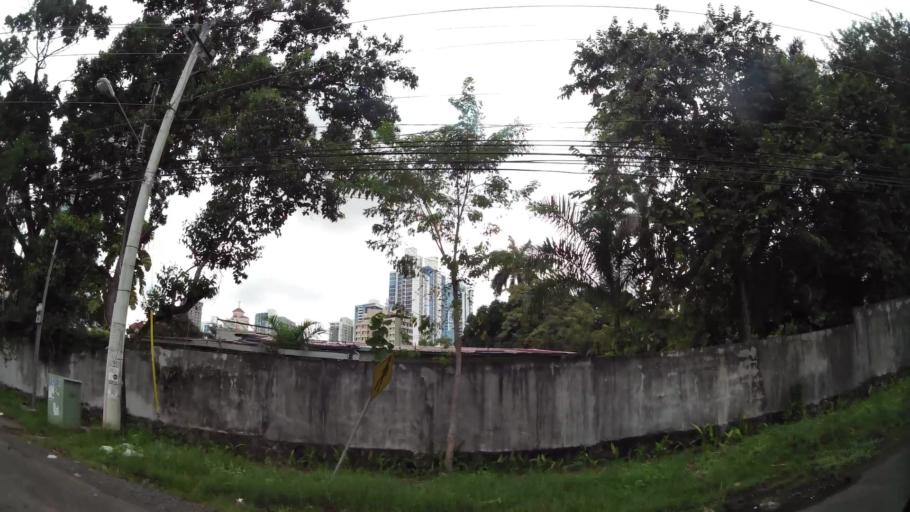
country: PA
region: Panama
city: Panama
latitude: 8.9980
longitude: -79.5035
